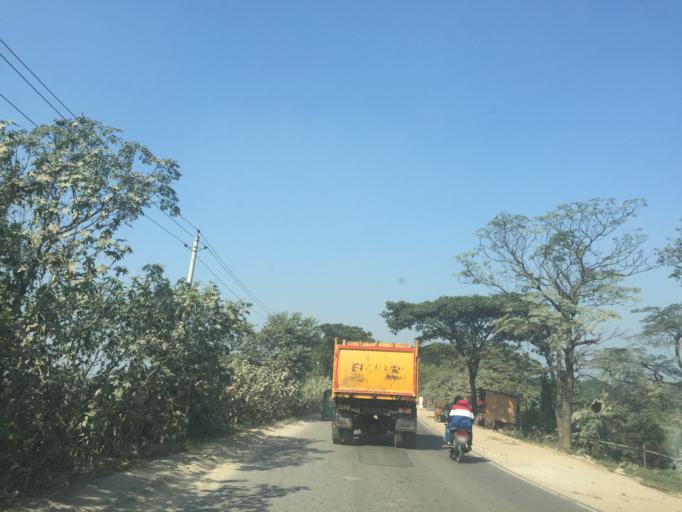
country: BD
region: Dhaka
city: Tungi
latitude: 23.8290
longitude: 90.3431
